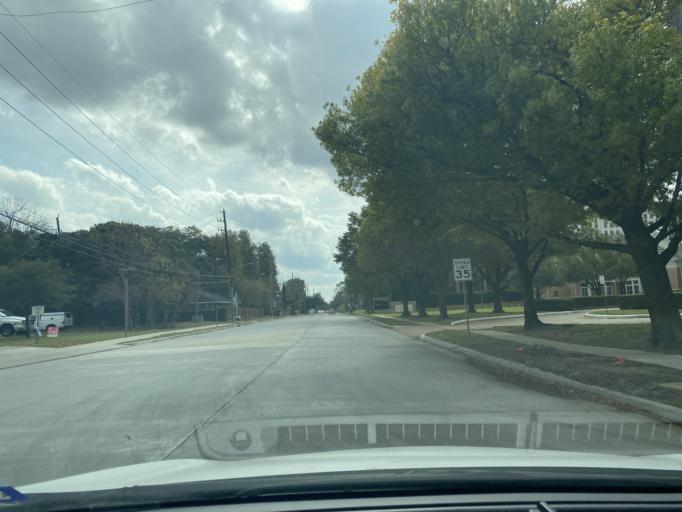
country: US
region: Texas
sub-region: Harris County
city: Hunters Creek Village
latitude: 29.7491
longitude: -95.4709
